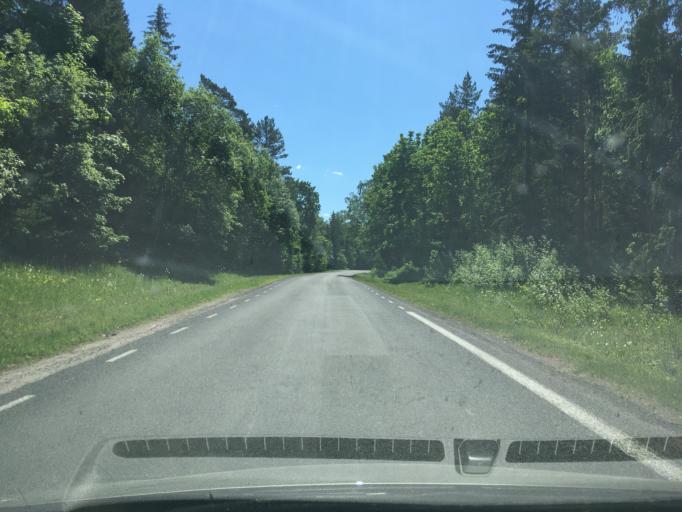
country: EE
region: Raplamaa
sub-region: Kohila vald
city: Kohila
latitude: 59.1577
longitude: 24.8517
